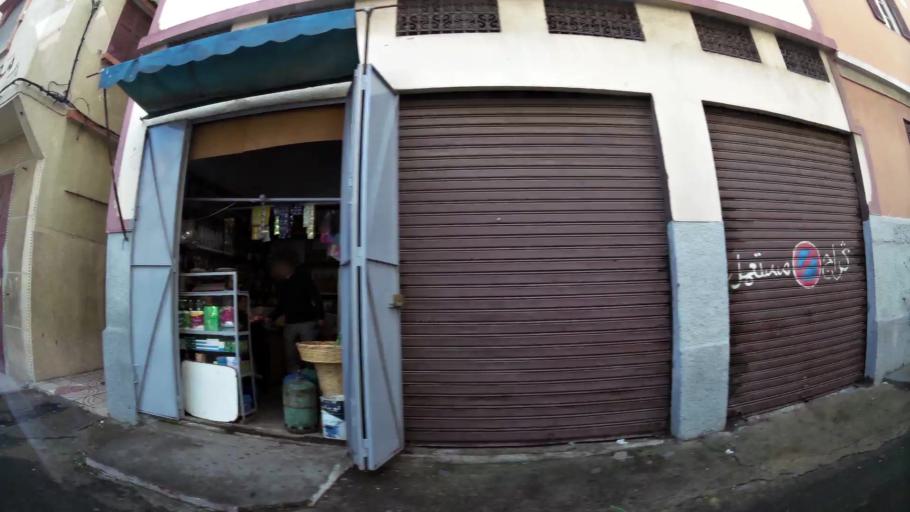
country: MA
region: Grand Casablanca
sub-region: Casablanca
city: Casablanca
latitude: 33.5497
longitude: -7.5984
